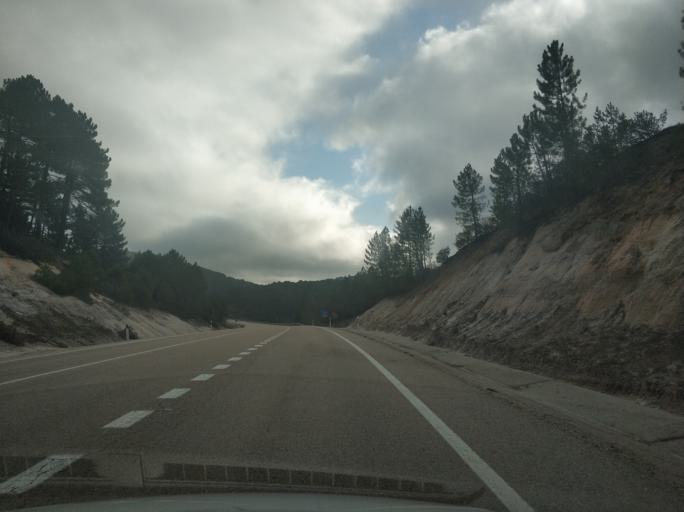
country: ES
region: Castille and Leon
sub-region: Provincia de Soria
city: Navaleno
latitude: 41.8302
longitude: -2.9775
